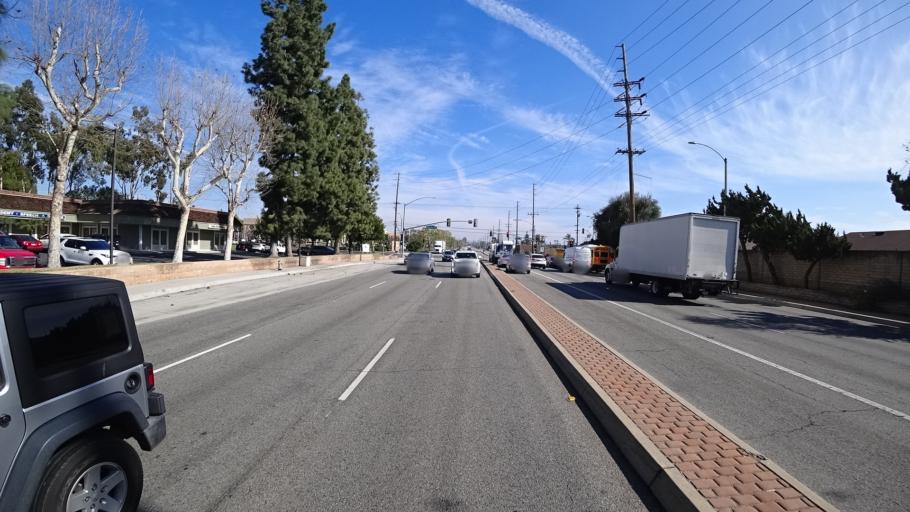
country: US
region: California
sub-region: Orange County
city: Brea
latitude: 33.9174
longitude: -117.9164
